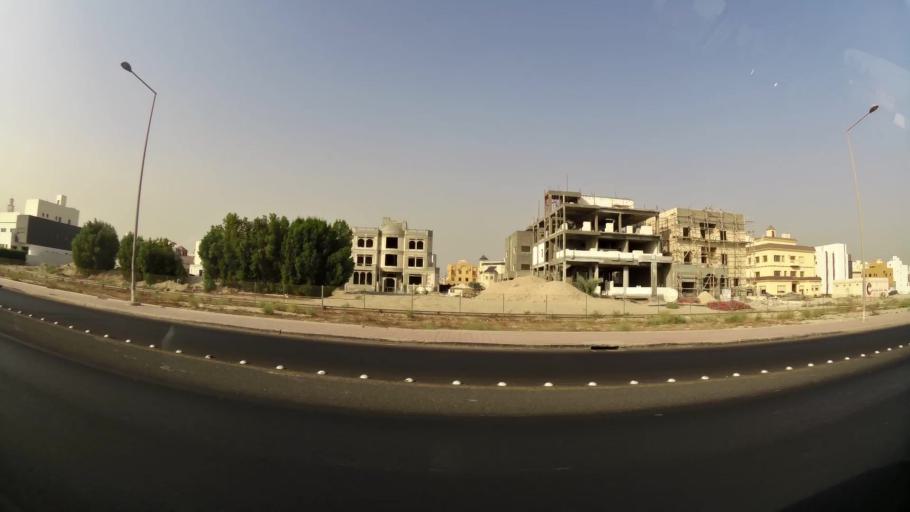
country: KW
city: Al Funaytis
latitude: 29.2358
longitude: 48.0959
